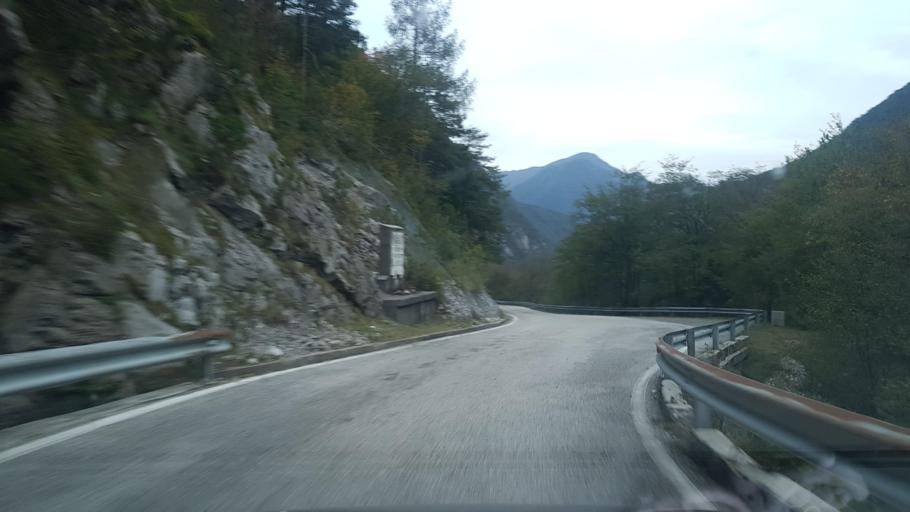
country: IT
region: Friuli Venezia Giulia
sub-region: Provincia di Udine
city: Villa Santina
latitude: 46.3390
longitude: 12.9315
